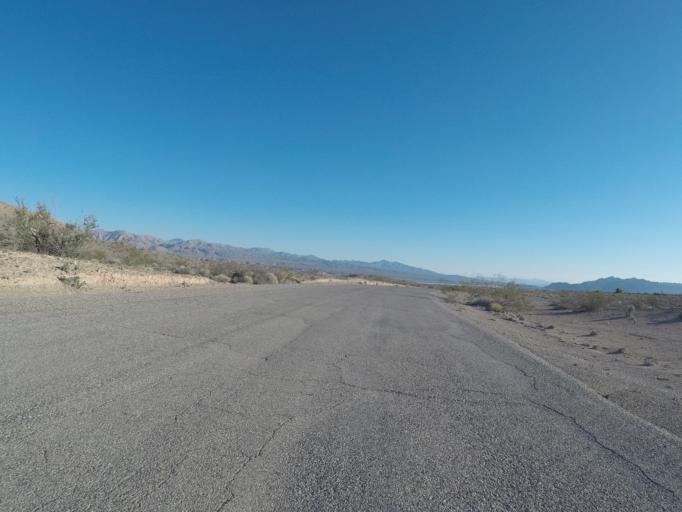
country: US
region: Nevada
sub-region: Clark County
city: Moapa Valley
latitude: 36.3936
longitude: -114.4233
